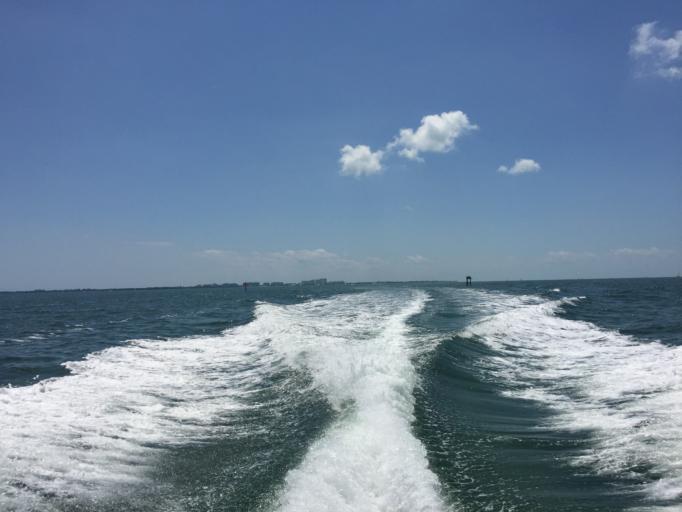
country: US
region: Florida
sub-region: Miami-Dade County
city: Coconut Grove
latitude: 25.7219
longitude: -80.2178
